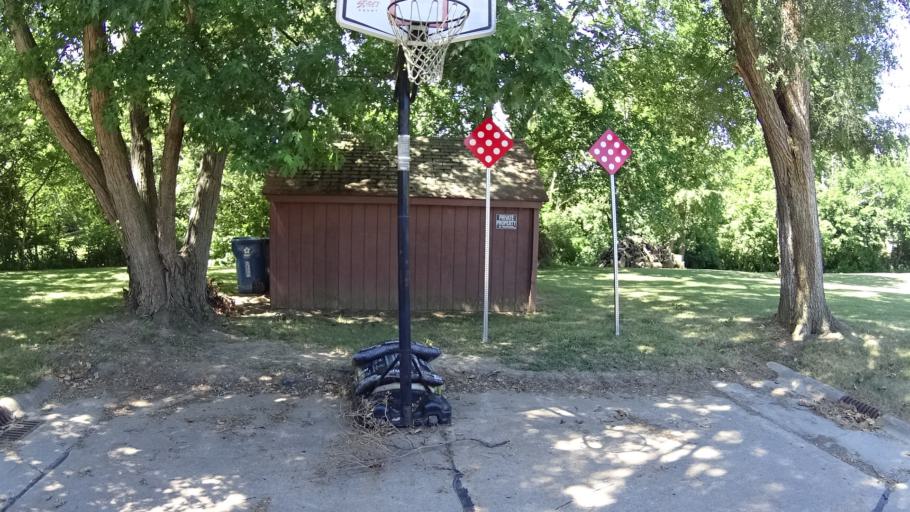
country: US
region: Ohio
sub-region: Erie County
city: Sandusky
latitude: 41.4111
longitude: -82.6935
